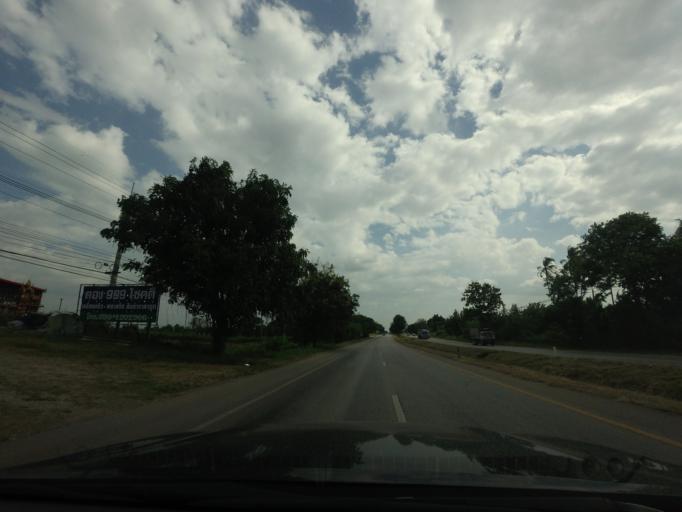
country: TH
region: Lop Buri
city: Chai Badan
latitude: 15.2393
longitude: 101.1264
